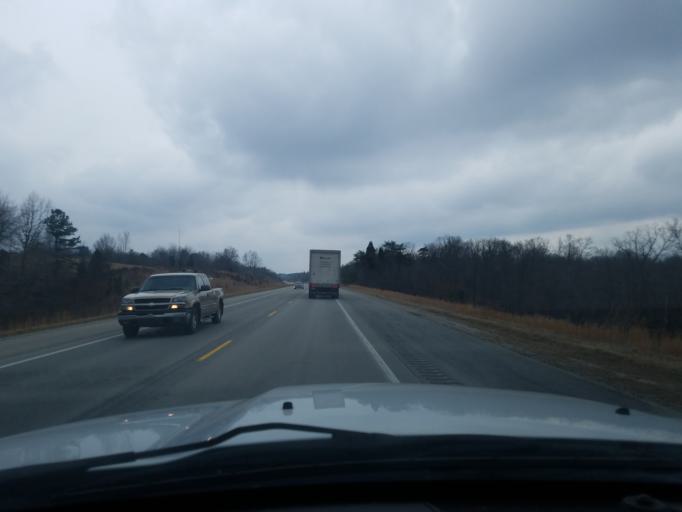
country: US
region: Indiana
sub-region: Perry County
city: Tell City
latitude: 38.0845
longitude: -86.6135
